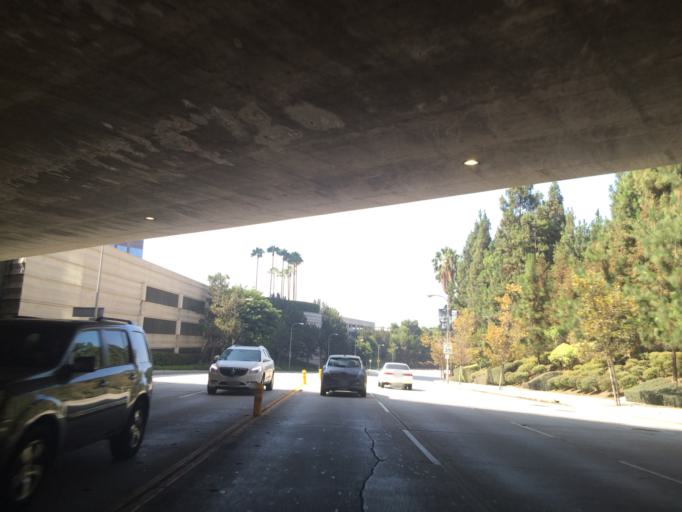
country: US
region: California
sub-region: Los Angeles County
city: Century City
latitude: 34.0564
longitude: -118.4137
